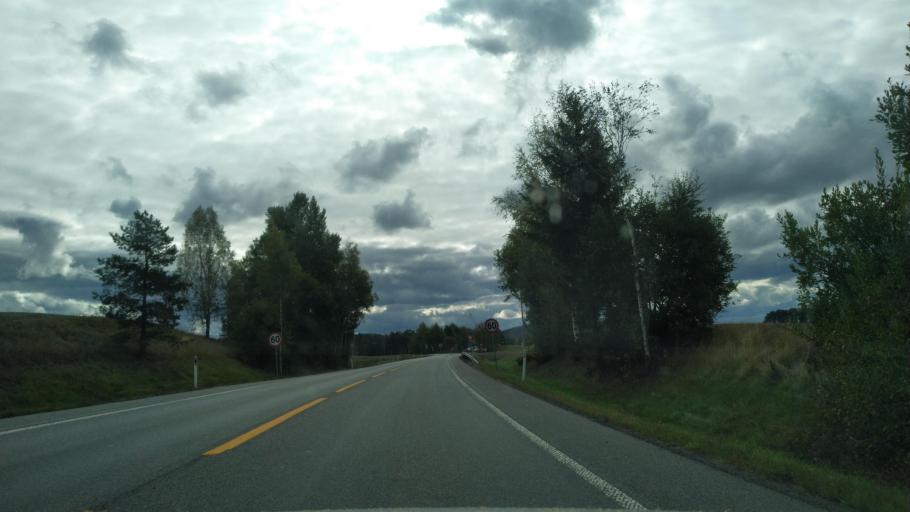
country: NO
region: Akershus
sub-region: Sorum
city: Frogner
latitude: 60.0326
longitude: 11.1130
